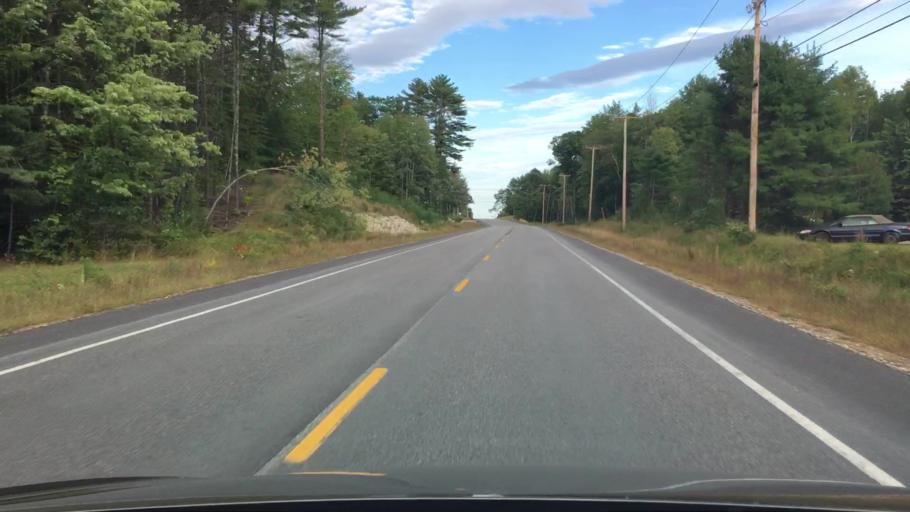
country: US
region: Maine
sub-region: Oxford County
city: Lovell
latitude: 44.0645
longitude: -70.8299
